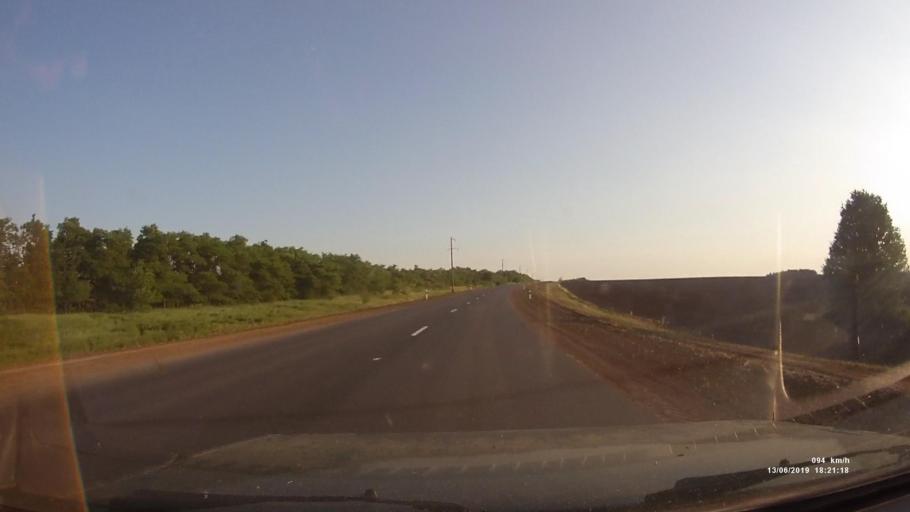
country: RU
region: Rostov
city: Kazanskaya
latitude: 49.8723
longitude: 41.2928
